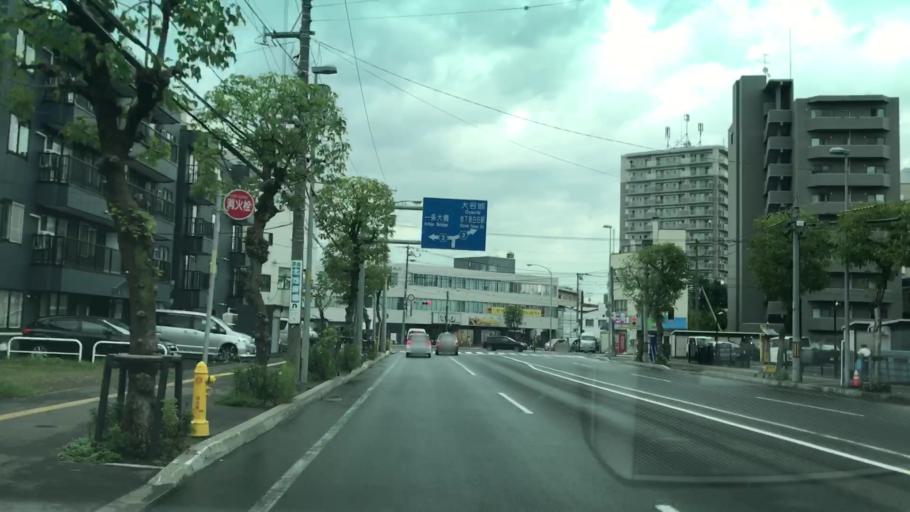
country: JP
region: Hokkaido
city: Sapporo
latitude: 43.0546
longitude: 141.3744
